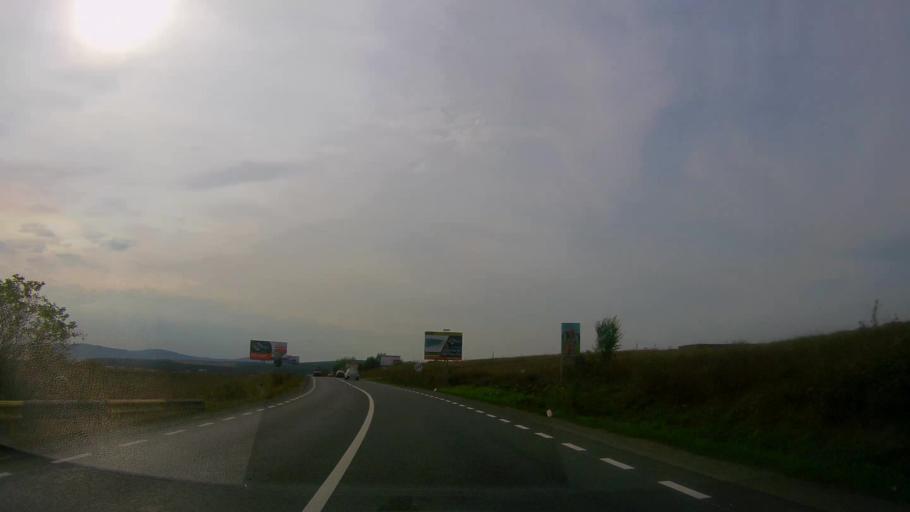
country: RO
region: Salaj
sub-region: Comuna Hereclean
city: Hereclean
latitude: 47.2383
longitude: 22.9930
